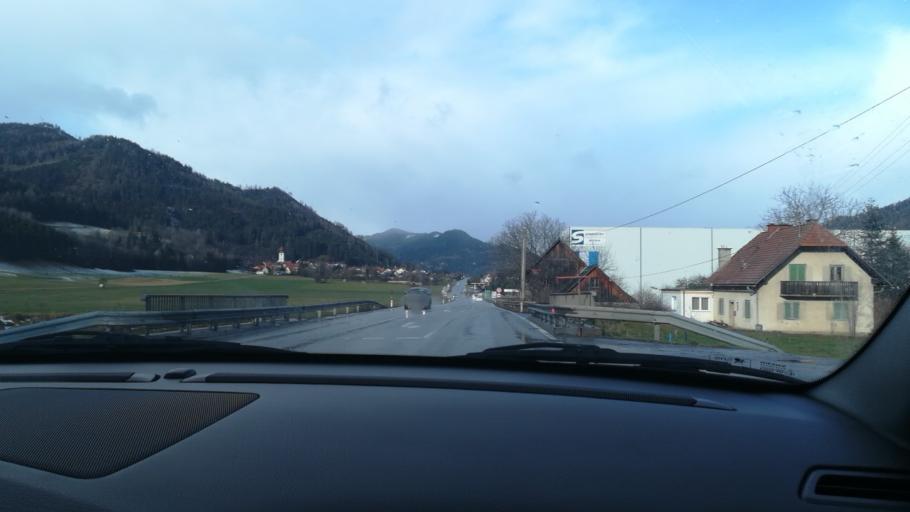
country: AT
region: Styria
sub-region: Politischer Bezirk Murtal
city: Sankt Peter ob Judenburg
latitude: 47.1803
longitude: 14.6019
